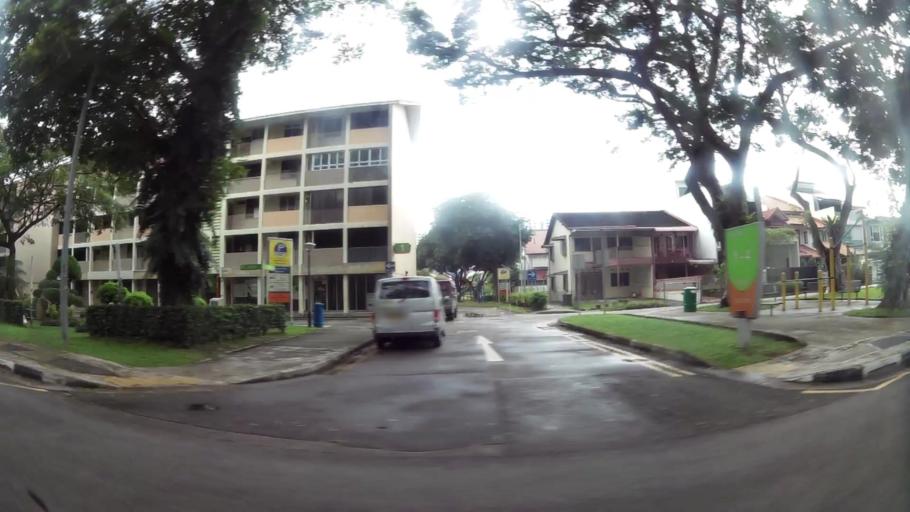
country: SG
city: Singapore
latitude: 1.3119
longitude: 103.9227
